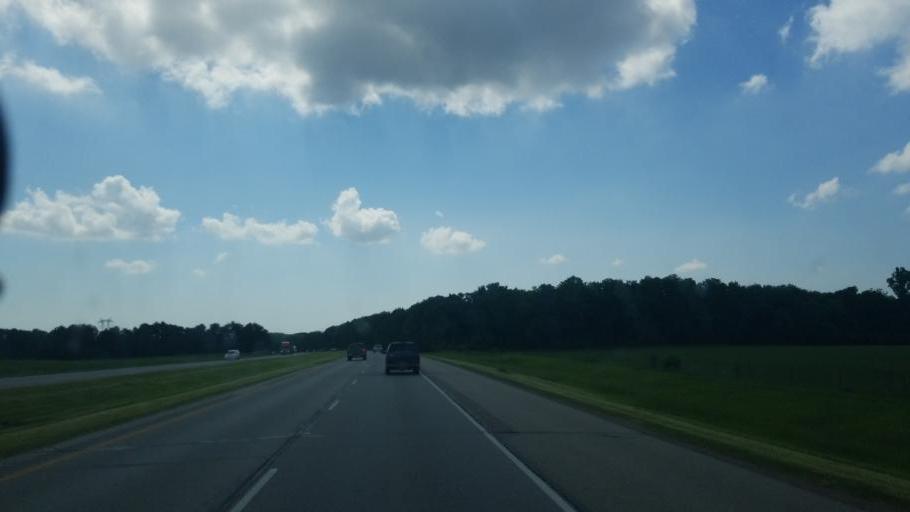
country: US
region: Indiana
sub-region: Kosciusko County
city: Warsaw
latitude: 41.2690
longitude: -85.9444
